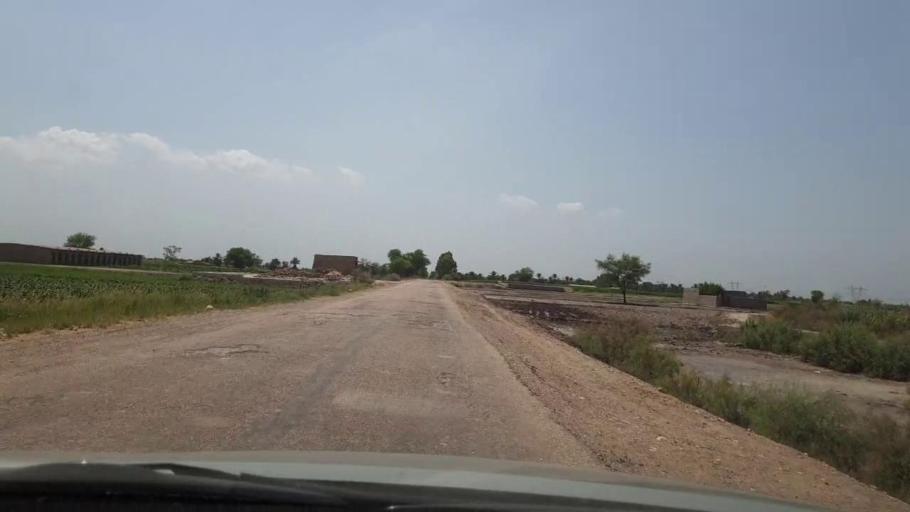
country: PK
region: Sindh
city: Rohri
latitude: 27.6695
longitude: 69.0653
